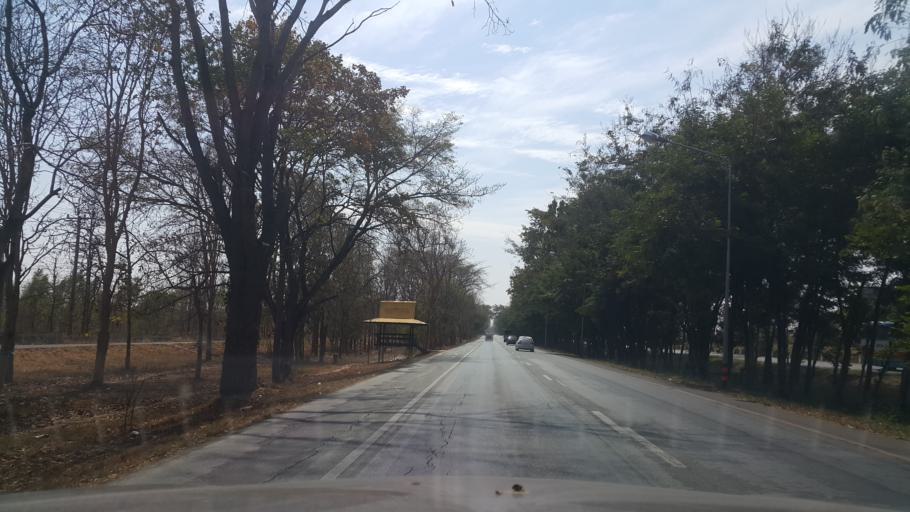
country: TH
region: Nakhon Ratchasima
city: Nakhon Ratchasima
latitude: 14.8820
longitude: 102.0717
